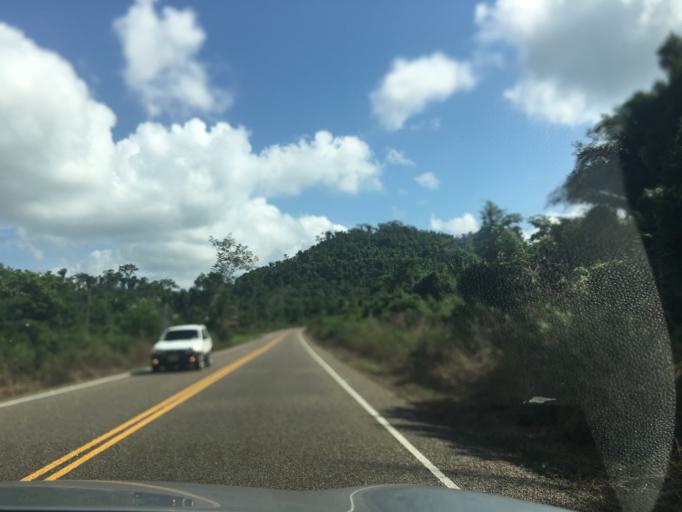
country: BZ
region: Cayo
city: Belmopan
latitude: 17.1585
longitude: -88.6875
